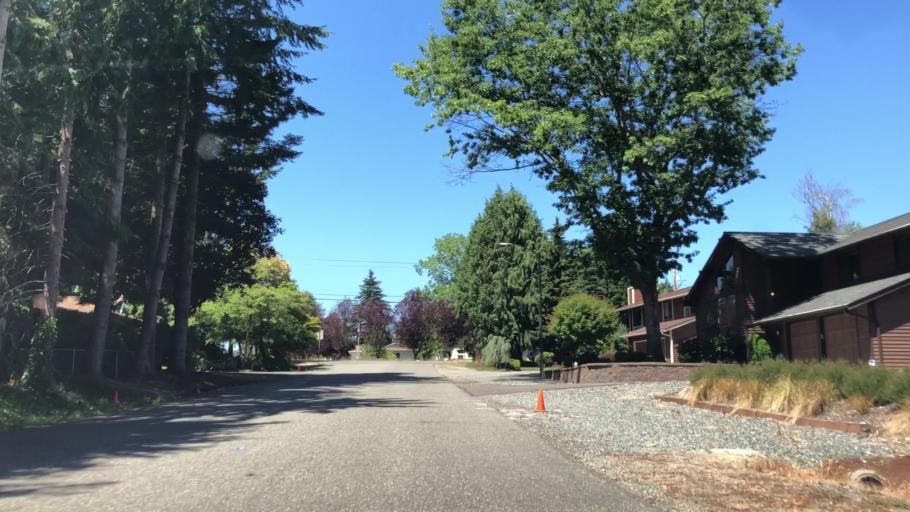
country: US
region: Washington
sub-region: Snohomish County
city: Martha Lake
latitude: 47.8591
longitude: -122.2455
